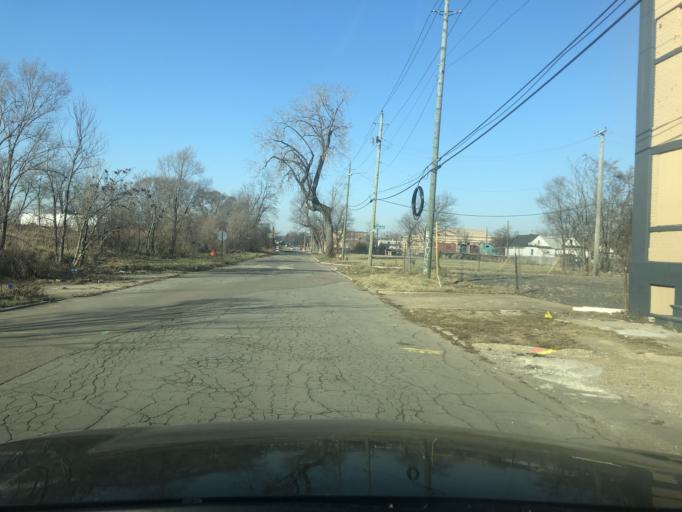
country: US
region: Michigan
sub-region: Wayne County
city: River Rouge
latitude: 42.3067
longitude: -83.0963
